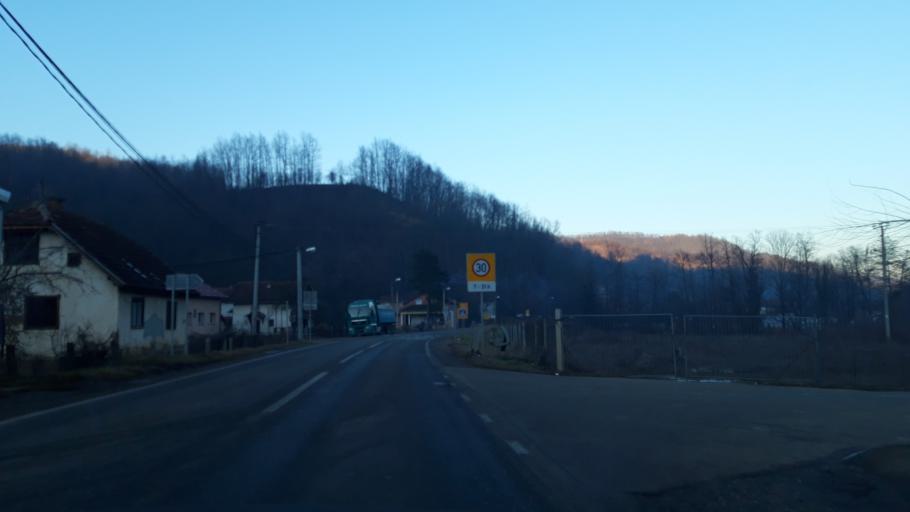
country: BA
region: Republika Srpska
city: Milici
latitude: 44.1929
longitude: 19.0718
